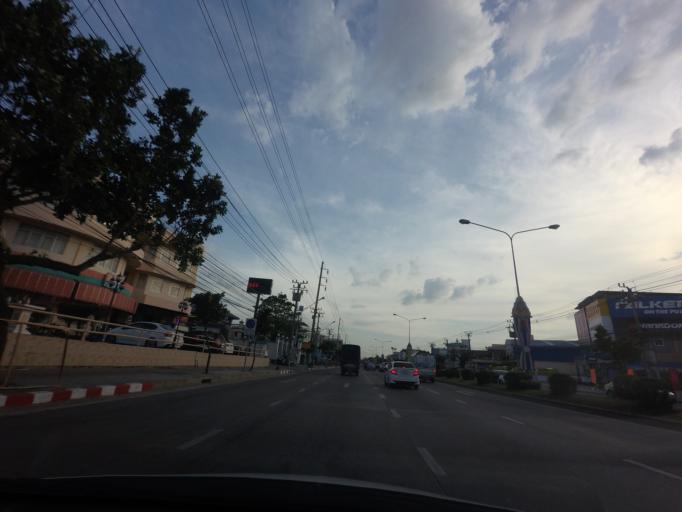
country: TH
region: Bangkok
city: Bang Khun Thian
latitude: 13.6356
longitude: 100.4332
